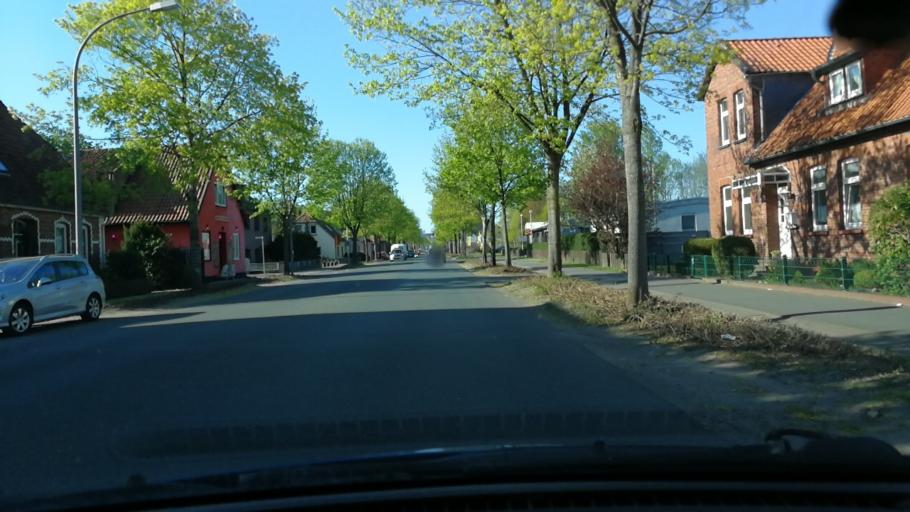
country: DE
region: Lower Saxony
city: Soltau
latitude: 52.9755
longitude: 9.8499
